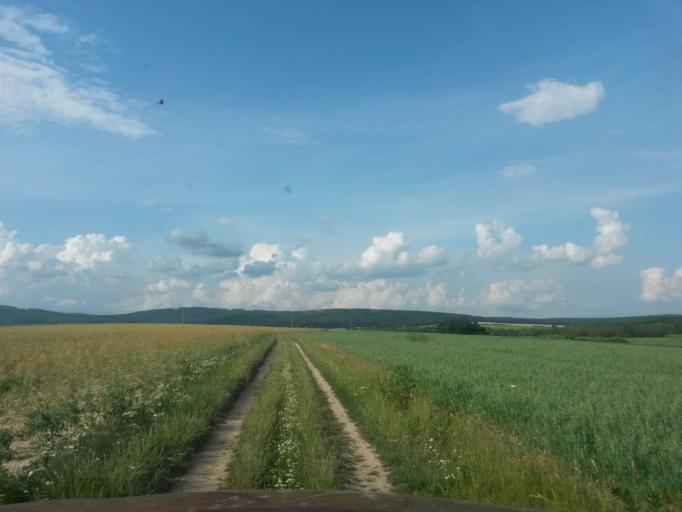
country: SK
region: Kosicky
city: Moldava nad Bodvou
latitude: 48.6545
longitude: 21.1070
